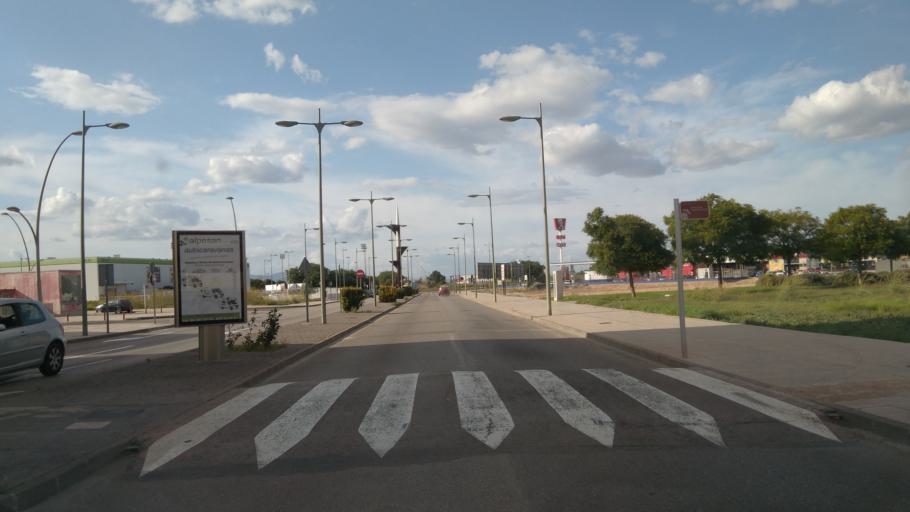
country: ES
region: Valencia
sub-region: Provincia de Valencia
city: Alzira
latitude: 39.1589
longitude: -0.4295
